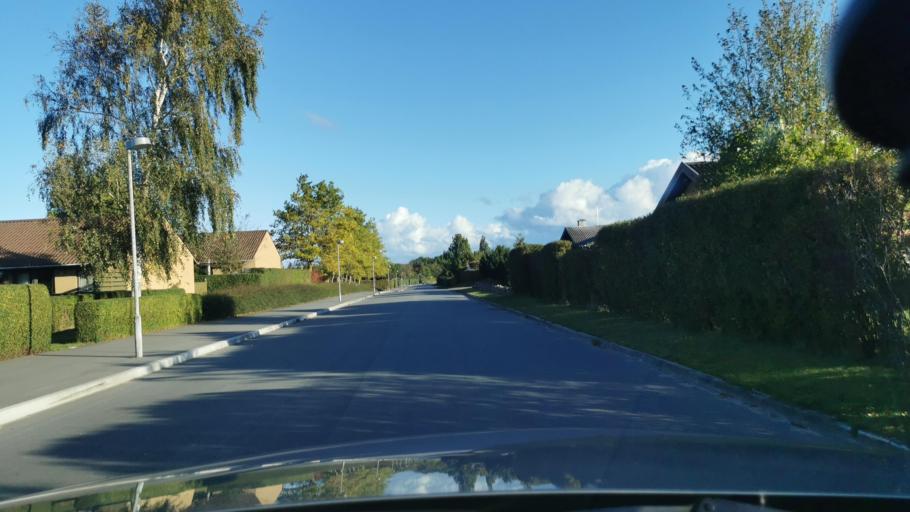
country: DK
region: Zealand
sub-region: Kalundborg Kommune
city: Svebolle
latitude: 55.6488
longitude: 11.2792
